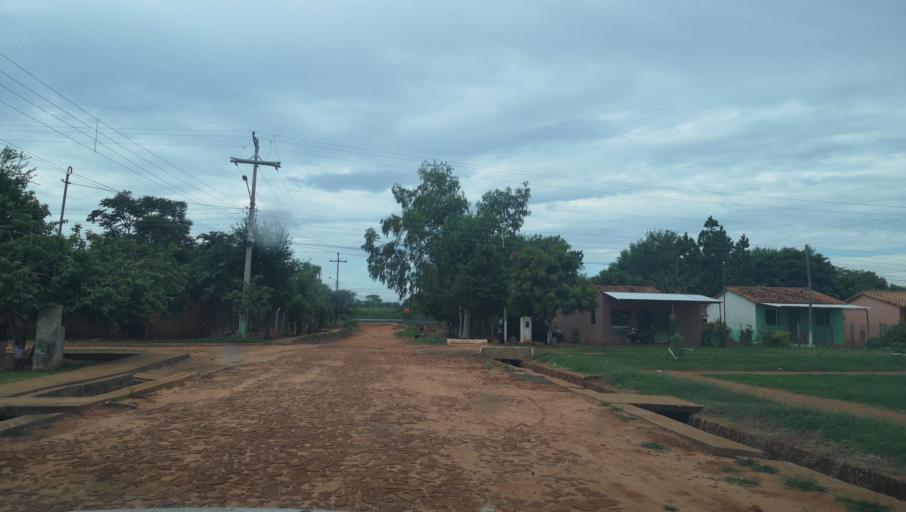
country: PY
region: San Pedro
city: Capiibary
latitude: -24.7426
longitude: -56.0333
